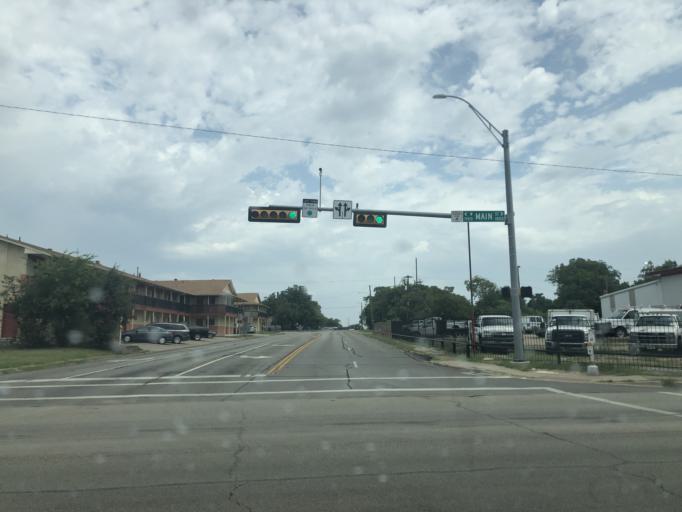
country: US
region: Texas
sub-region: Dallas County
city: Grand Prairie
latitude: 32.7405
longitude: -97.0291
